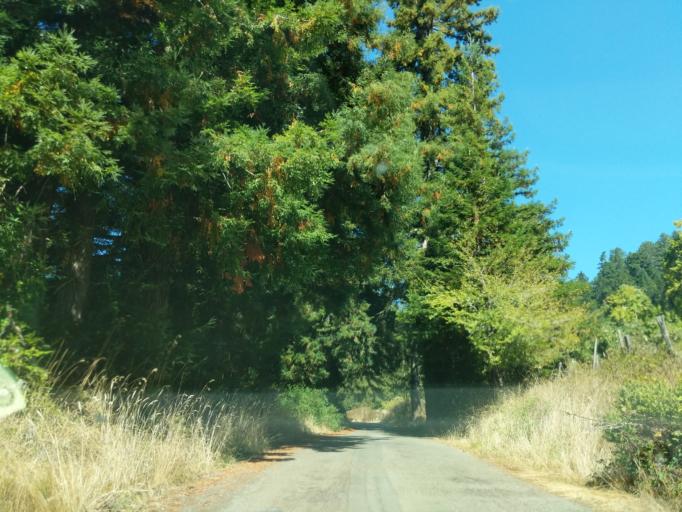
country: US
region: California
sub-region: Sonoma County
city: Monte Rio
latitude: 38.5227
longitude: -123.2416
